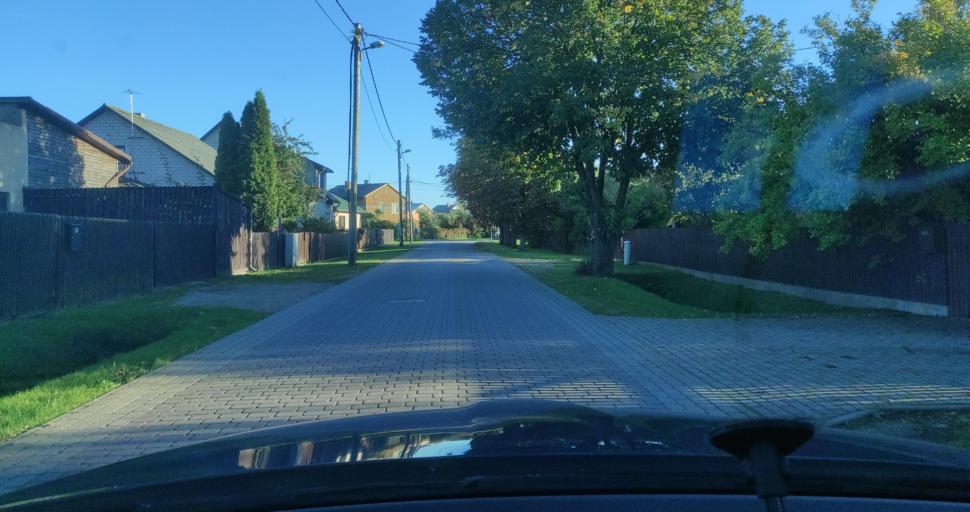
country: LV
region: Ventspils
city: Ventspils
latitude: 57.3745
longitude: 21.5770
